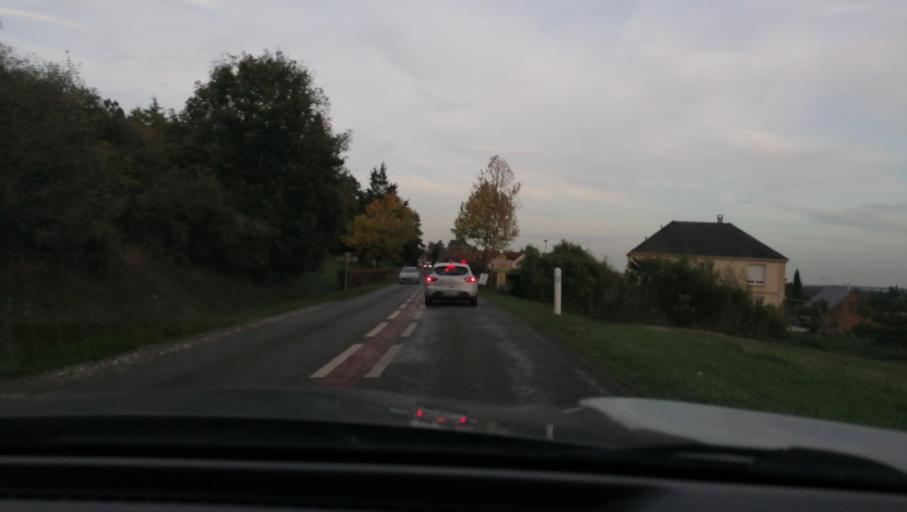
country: FR
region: Picardie
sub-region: Departement de la Somme
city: Ailly-sur-Somme
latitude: 49.8895
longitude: 2.1714
